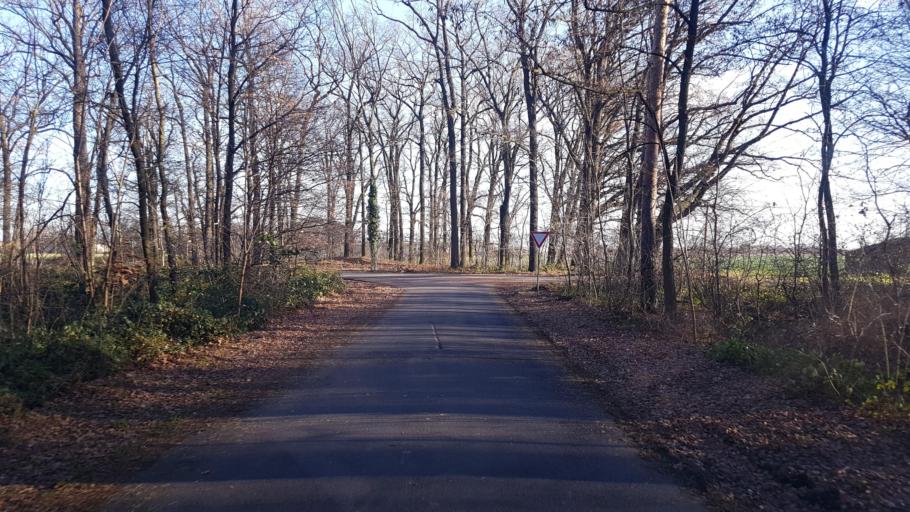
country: DE
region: Brandenburg
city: Forst
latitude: 51.7684
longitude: 14.6161
